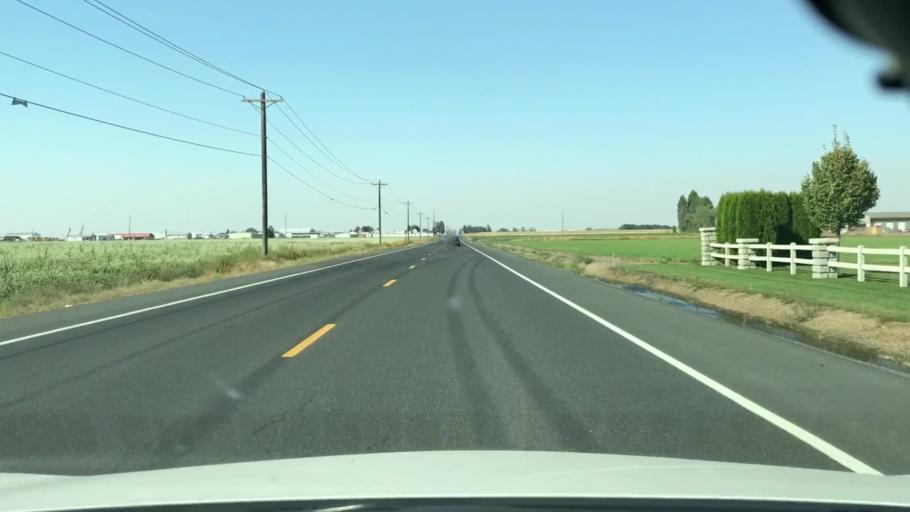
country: US
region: Washington
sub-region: Grant County
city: Moses Lake
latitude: 47.1253
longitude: -119.2358
